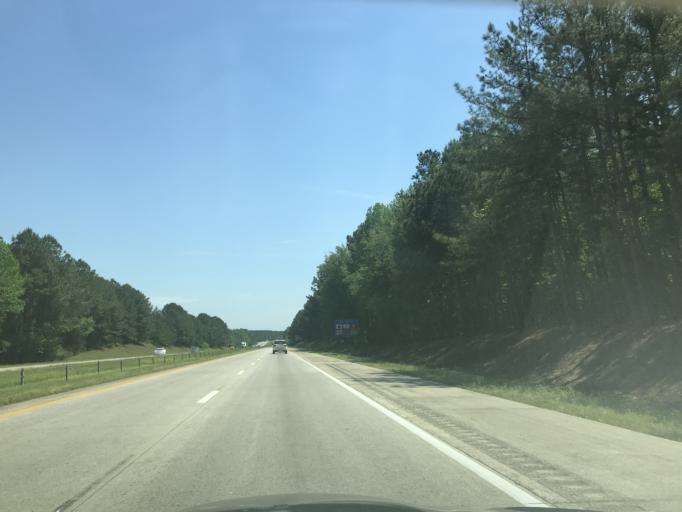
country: US
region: North Carolina
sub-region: Johnston County
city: Benson
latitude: 35.5266
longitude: -78.5651
